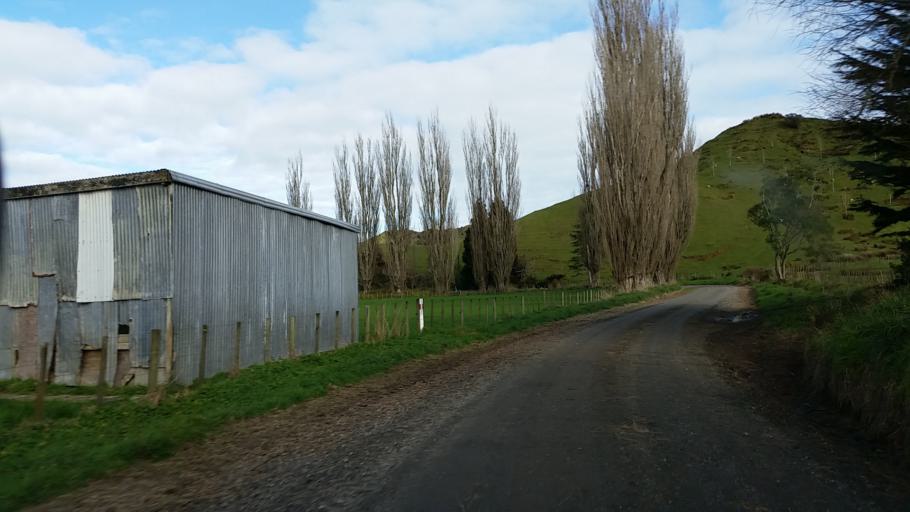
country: NZ
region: Taranaki
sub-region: South Taranaki District
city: Eltham
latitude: -39.2540
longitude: 174.5308
